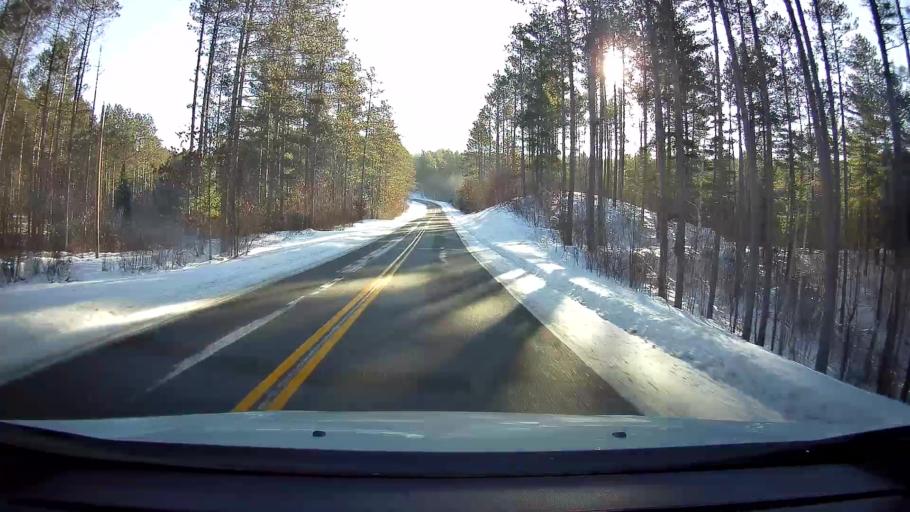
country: US
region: Wisconsin
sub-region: Sawyer County
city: Little Round Lake
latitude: 46.1105
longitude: -91.3048
